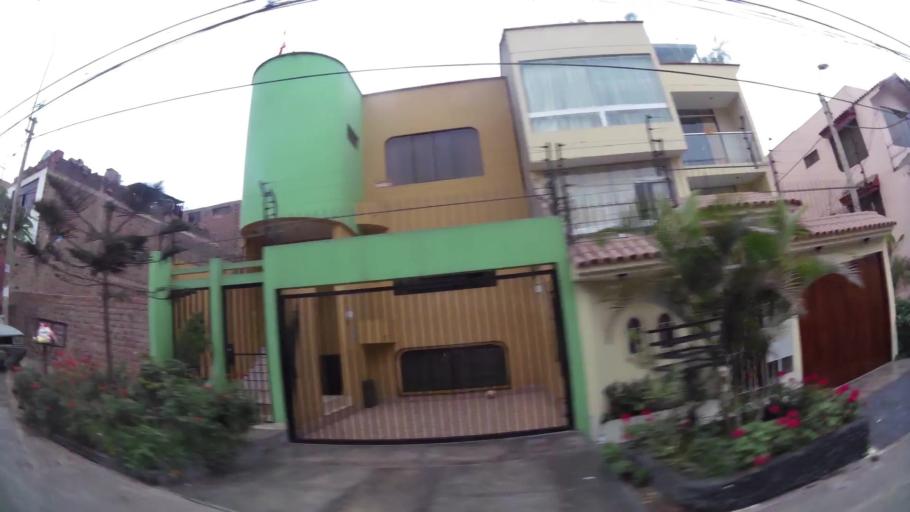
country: PE
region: Lima
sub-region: Lima
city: La Molina
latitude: -12.1131
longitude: -76.9382
